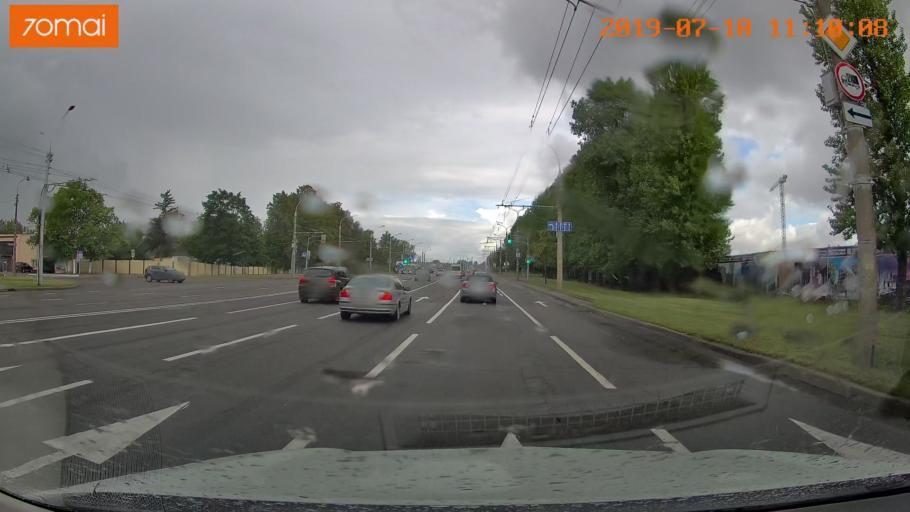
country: BY
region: Minsk
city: Syenitsa
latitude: 53.8650
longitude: 27.5304
